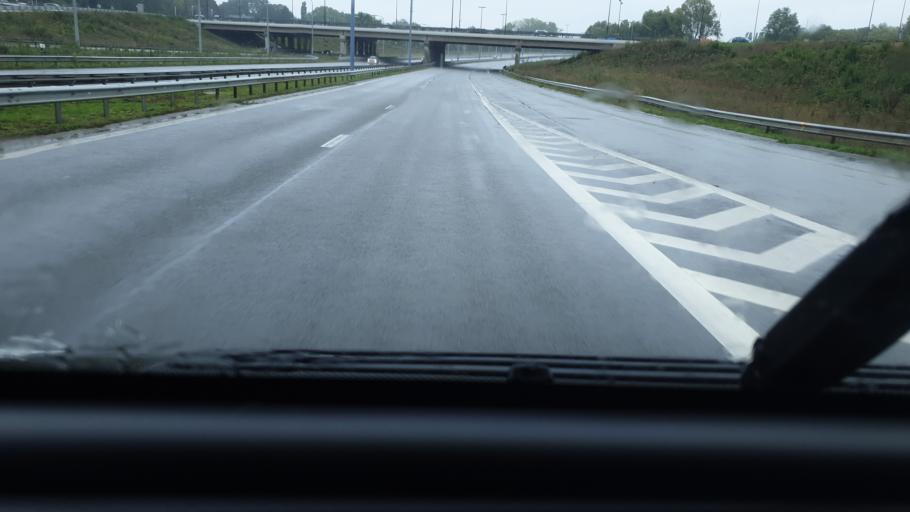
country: BE
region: Wallonia
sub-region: Province du Hainaut
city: Chatelet
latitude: 50.4198
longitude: 4.4980
